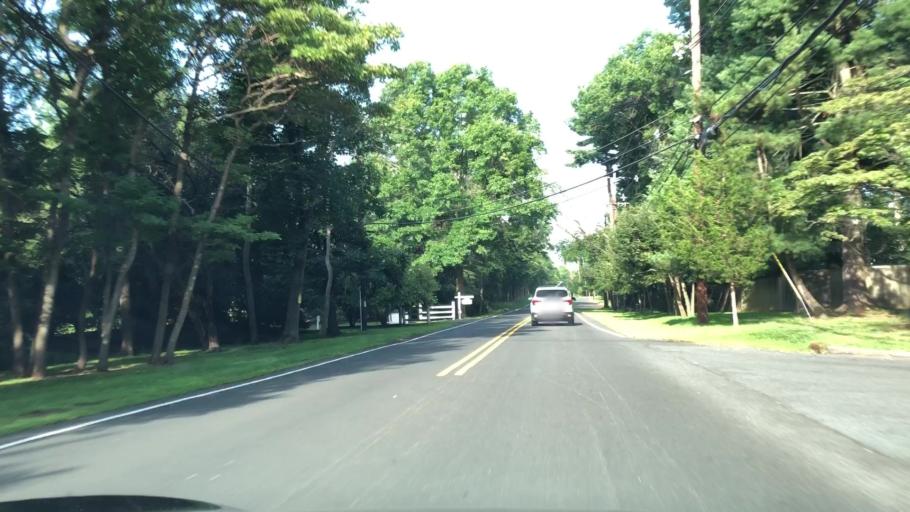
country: US
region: New Jersey
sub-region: Mercer County
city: Pennington
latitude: 40.3395
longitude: -74.7502
